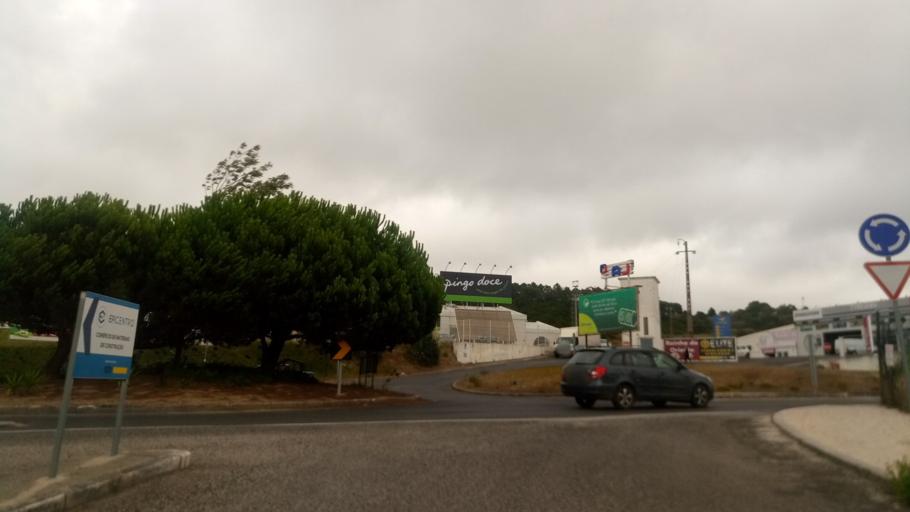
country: PT
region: Leiria
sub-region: Caldas da Rainha
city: Caldas da Rainha
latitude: 39.4262
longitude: -9.1312
